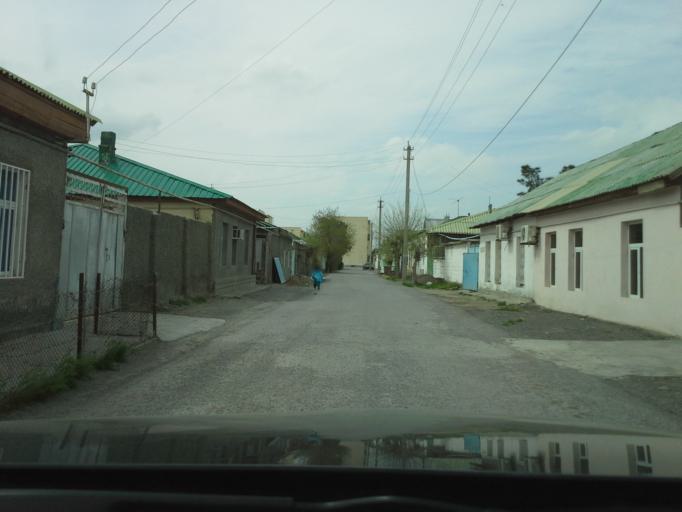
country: TM
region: Ahal
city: Abadan
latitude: 38.0623
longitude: 58.1535
